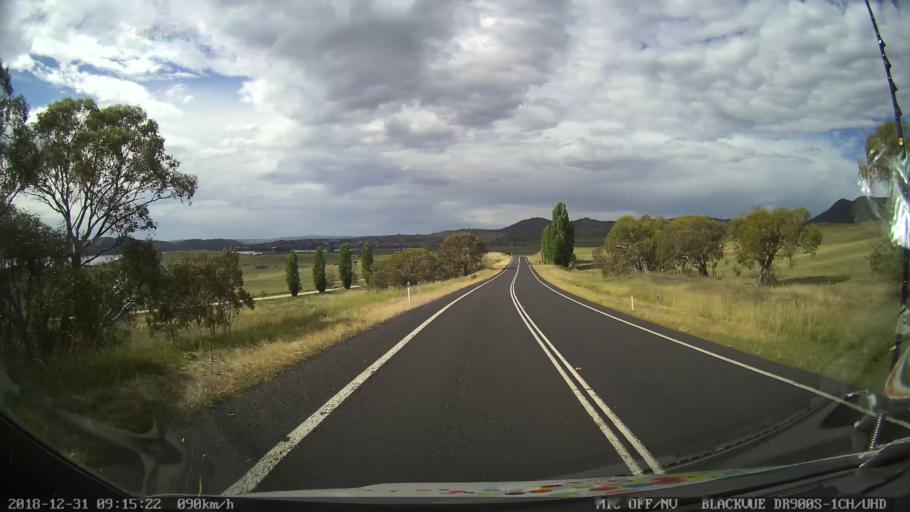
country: AU
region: New South Wales
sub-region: Snowy River
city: Jindabyne
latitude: -36.3843
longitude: 148.5995
